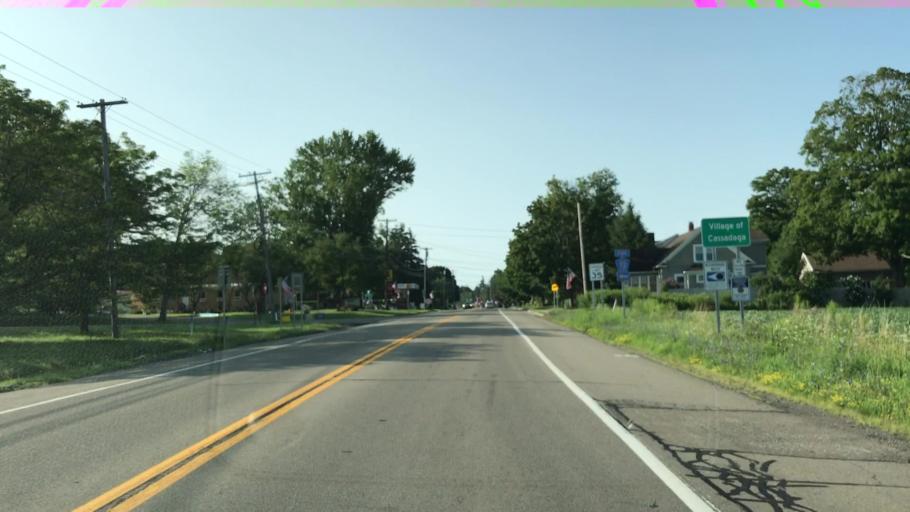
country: US
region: New York
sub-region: Chautauqua County
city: Fredonia
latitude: 42.3493
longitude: -79.3107
